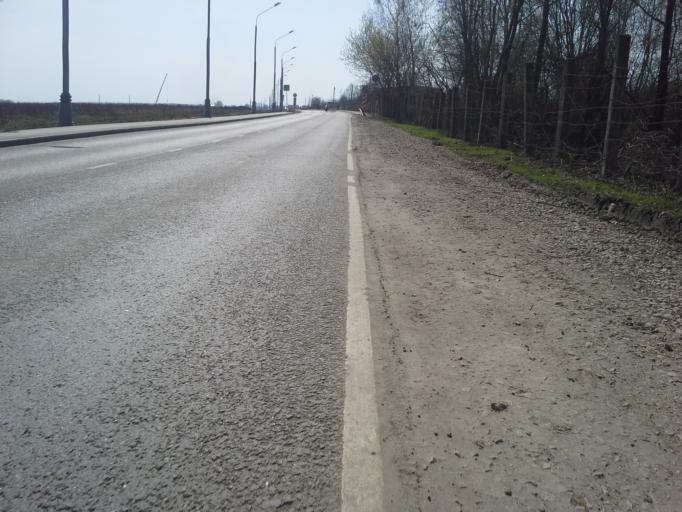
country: RU
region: Moskovskaya
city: Shcherbinka
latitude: 55.5068
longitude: 37.5259
